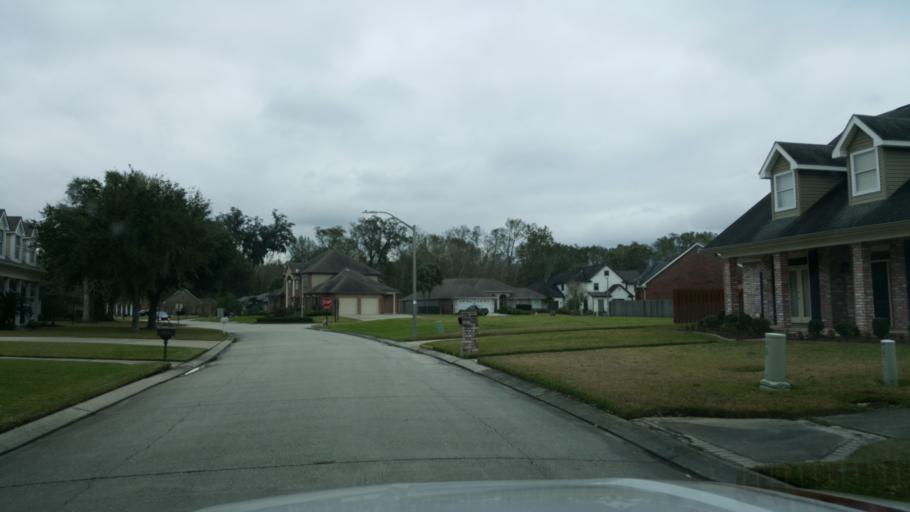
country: US
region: Louisiana
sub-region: Jefferson Parish
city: Woodmere
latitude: 29.8741
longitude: -90.0806
